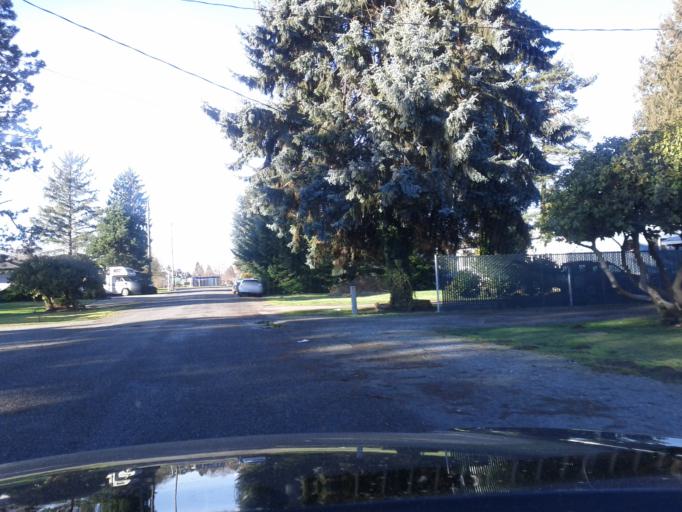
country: US
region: Washington
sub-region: Skagit County
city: Burlington
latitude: 48.4612
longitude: -122.3232
